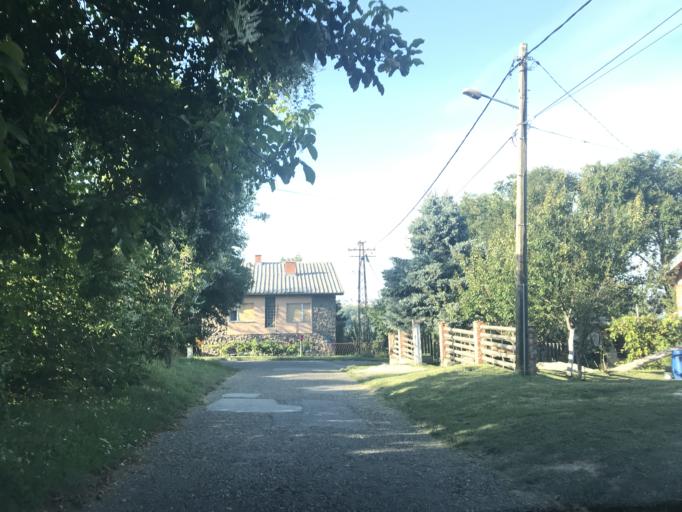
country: RS
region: Autonomna Pokrajina Vojvodina
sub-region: Juznobacki Okrug
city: Novi Sad
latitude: 45.2113
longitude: 19.8027
